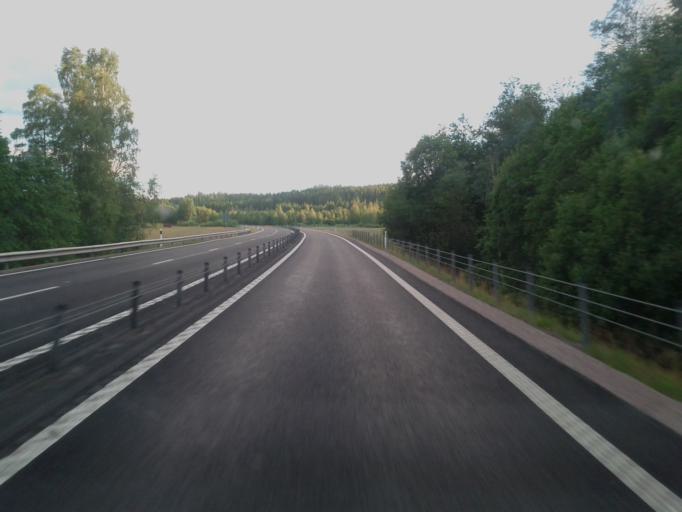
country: SE
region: Dalarna
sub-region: Borlange Kommun
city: Borlaenge
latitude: 60.4590
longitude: 15.3765
